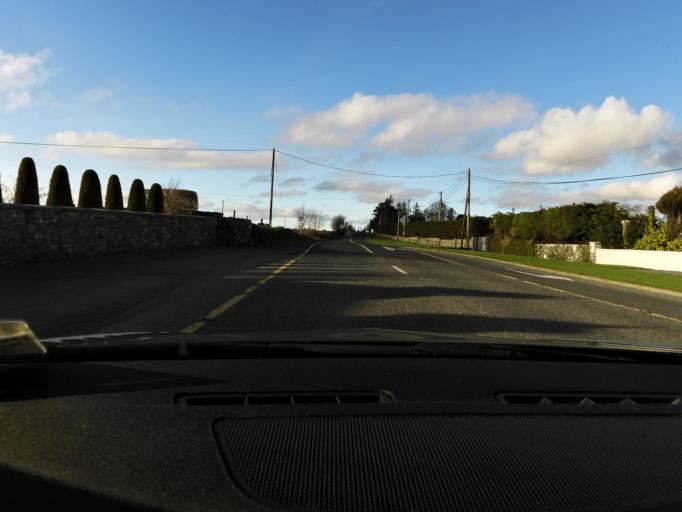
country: IE
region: Connaught
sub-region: Roscommon
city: Roscommon
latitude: 53.6777
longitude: -8.1974
